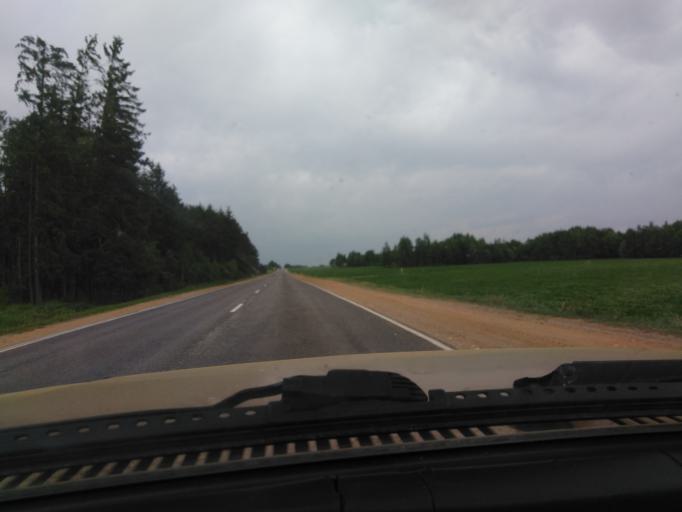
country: BY
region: Mogilev
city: Kamyennyya Lavy
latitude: 54.0457
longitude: 30.3253
